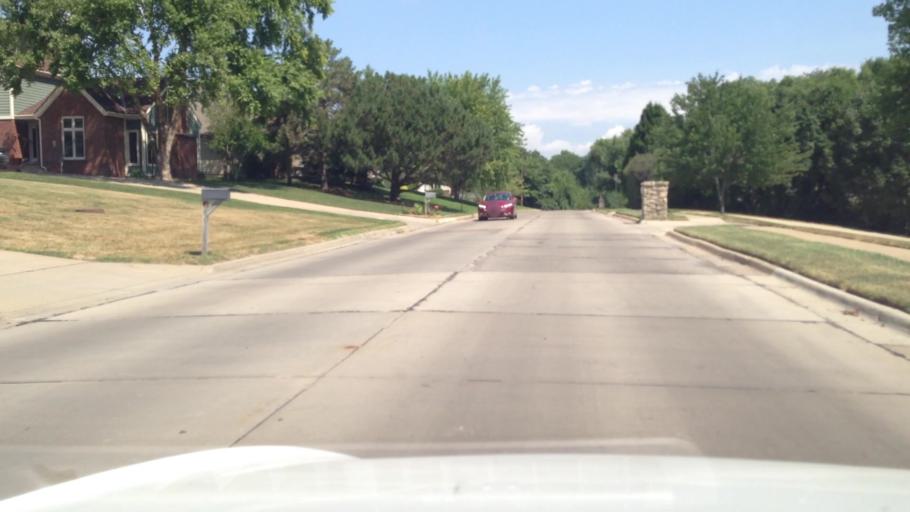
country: US
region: Kansas
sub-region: Douglas County
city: Lawrence
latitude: 38.9448
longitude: -95.2980
